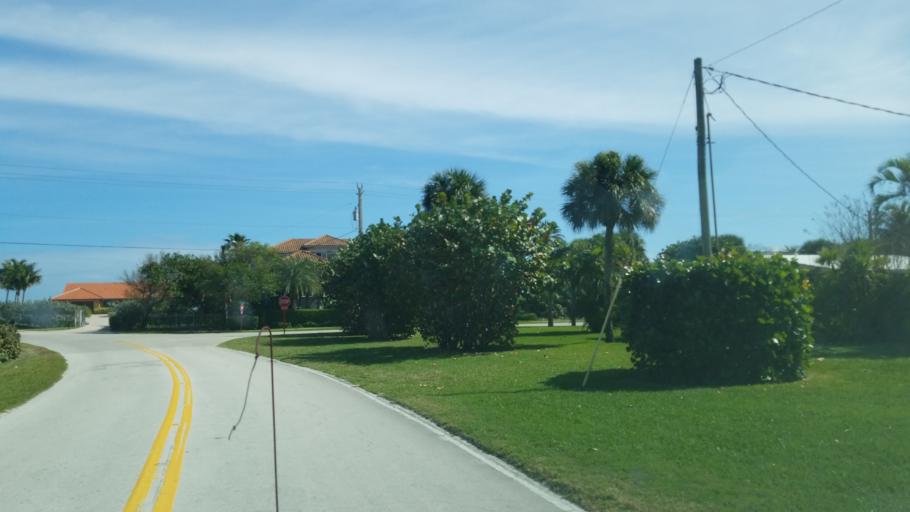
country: US
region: Florida
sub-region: Indian River County
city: Vero Beach
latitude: 27.6596
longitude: -80.3591
